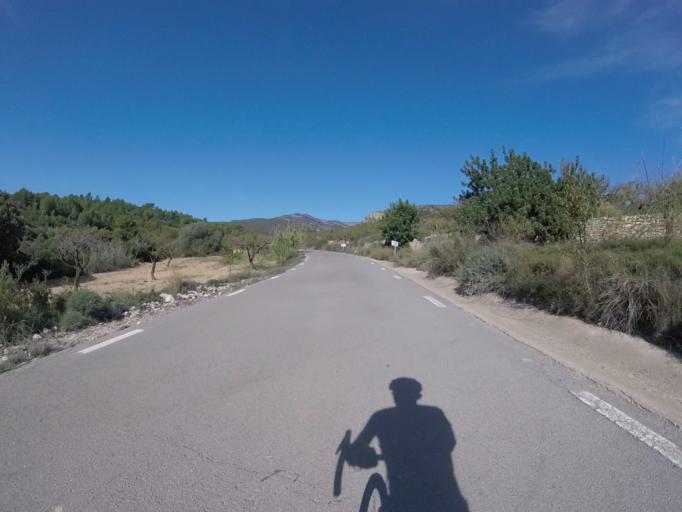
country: ES
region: Valencia
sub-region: Provincia de Castello
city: Sarratella
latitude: 40.2727
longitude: 0.0379
